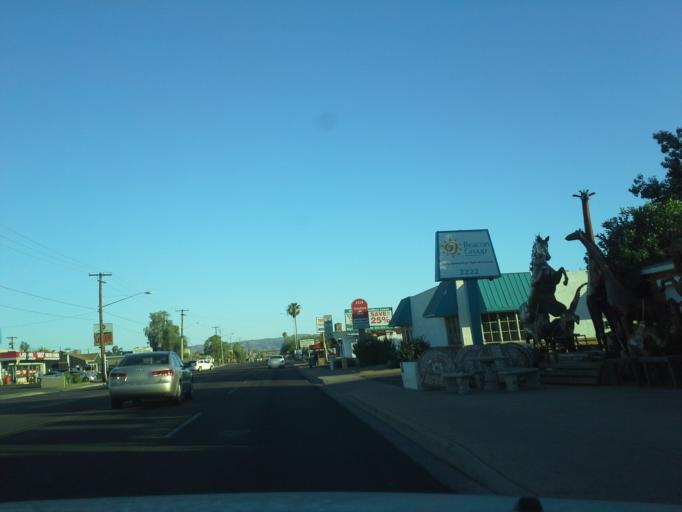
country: US
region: Arizona
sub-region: Maricopa County
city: Phoenix
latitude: 33.4725
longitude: -112.0303
